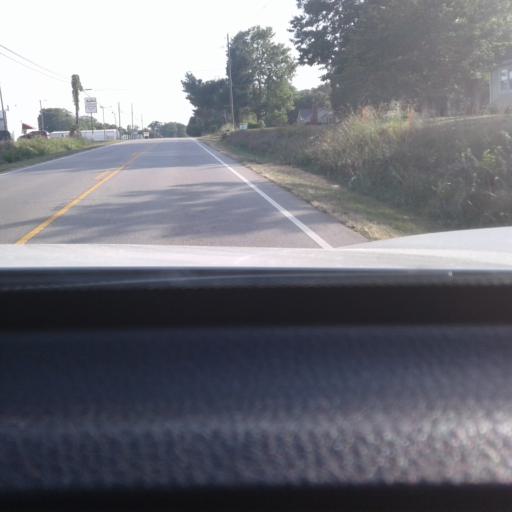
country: US
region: North Carolina
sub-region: Harnett County
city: Dunn
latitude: 35.3233
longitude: -78.6037
